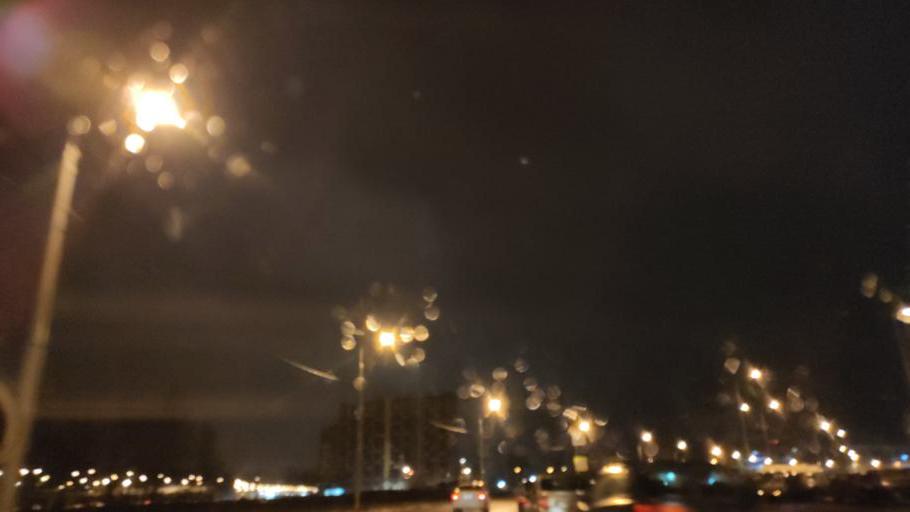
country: RU
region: Moskovskaya
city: Vatutinki
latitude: 55.5145
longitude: 37.3583
